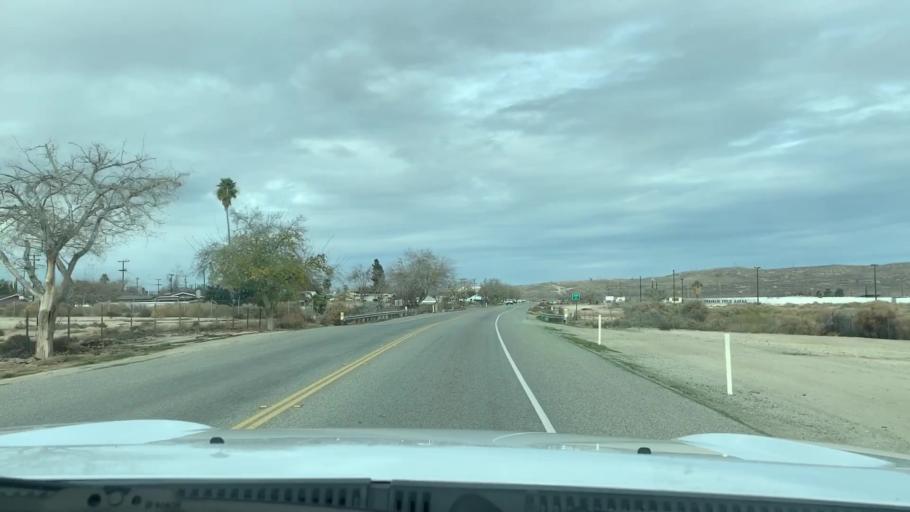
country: US
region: California
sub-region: Kern County
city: Ford City
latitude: 35.1494
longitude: -119.4477
